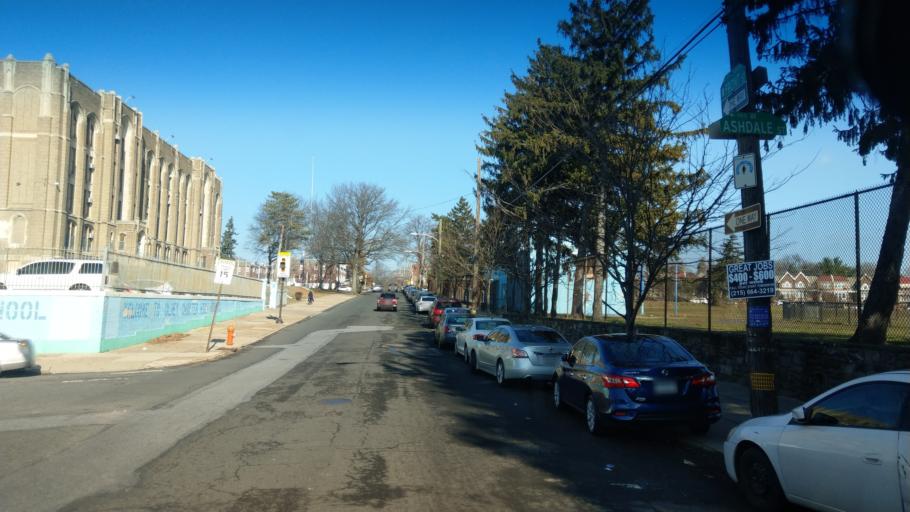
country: US
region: Pennsylvania
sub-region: Montgomery County
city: Rockledge
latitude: 40.0275
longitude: -75.1231
